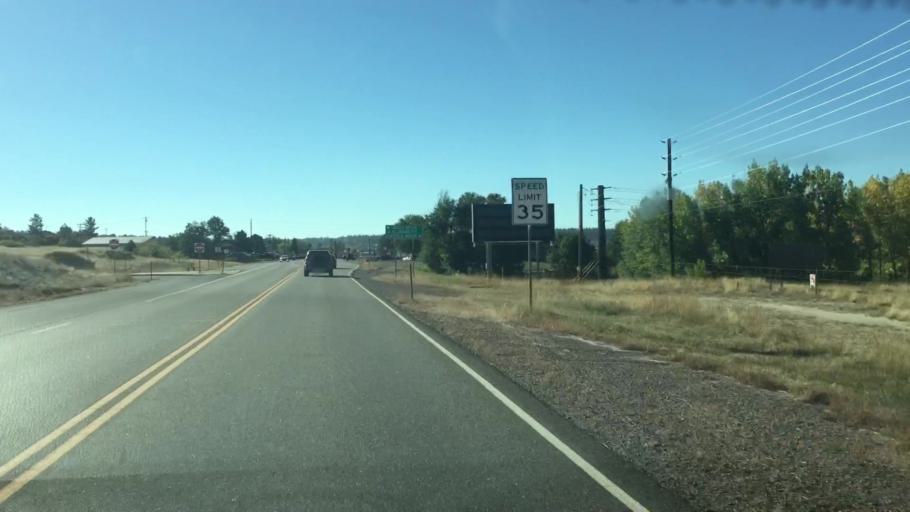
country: US
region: Colorado
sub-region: Douglas County
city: The Pinery
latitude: 39.3957
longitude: -104.7546
